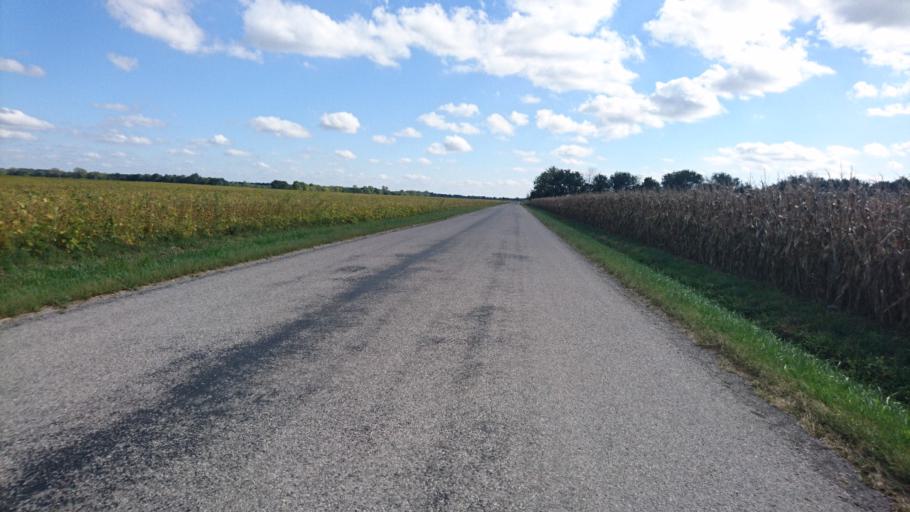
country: US
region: Illinois
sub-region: Macoupin County
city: Mount Olive
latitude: 39.0191
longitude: -89.7315
